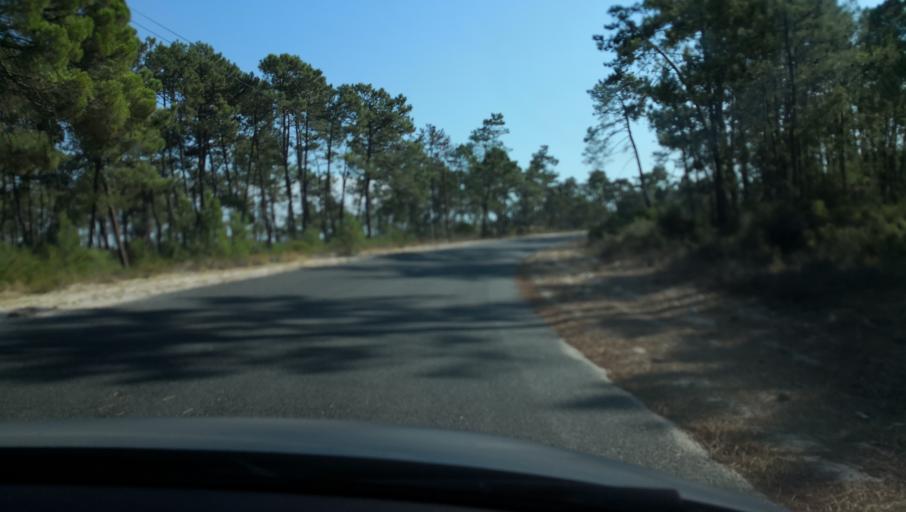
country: PT
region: Setubal
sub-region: Setubal
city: Setubal
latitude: 38.4679
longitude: -8.8696
